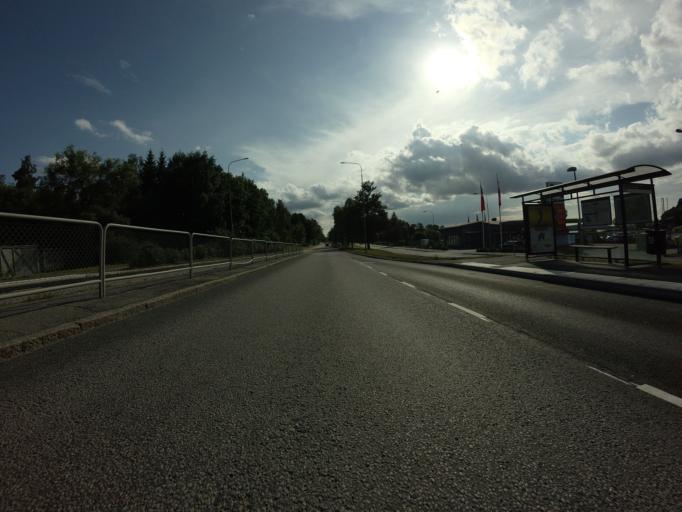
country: SE
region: Stockholm
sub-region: Lidingo
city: Lidingoe
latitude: 59.3692
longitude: 18.1211
